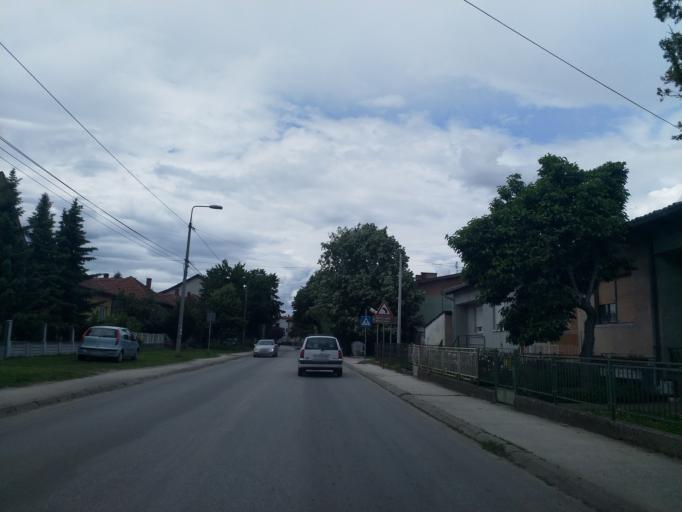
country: RS
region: Central Serbia
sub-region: Pomoravski Okrug
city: Jagodina
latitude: 43.9742
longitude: 21.2729
